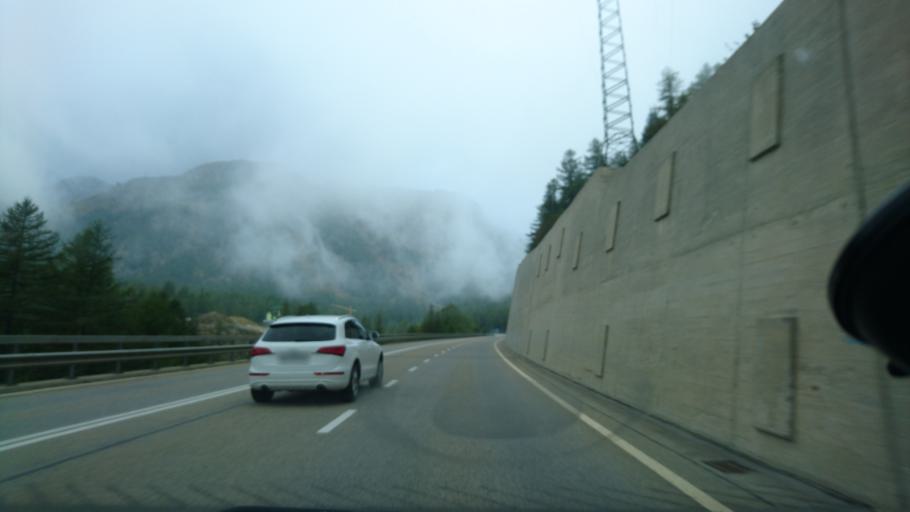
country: CH
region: Valais
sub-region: Brig District
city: Brig
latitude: 46.2013
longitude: 8.0524
